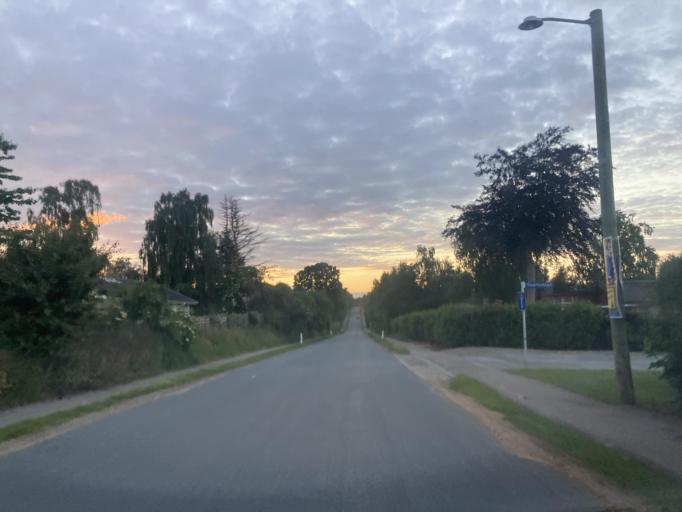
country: DK
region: Capital Region
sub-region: Gribskov Kommune
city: Helsinge
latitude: 56.0633
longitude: 12.1147
